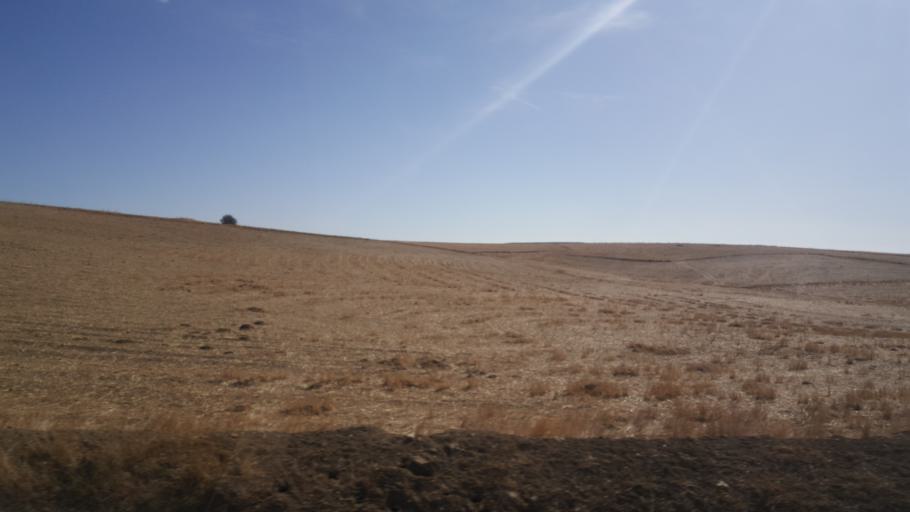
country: TR
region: Ankara
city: Yenice
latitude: 39.2912
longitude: 32.6313
